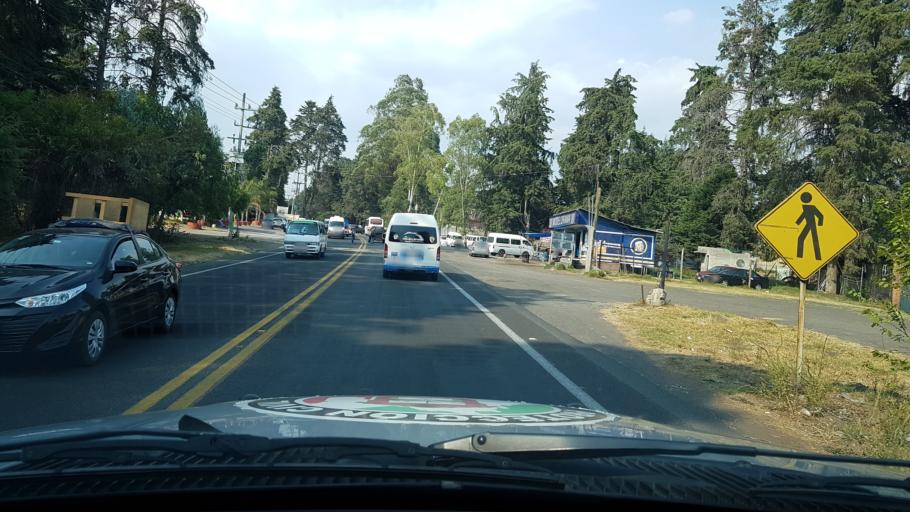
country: MX
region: Mexico
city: Ozumba de Alzate
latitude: 19.0546
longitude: -98.7884
